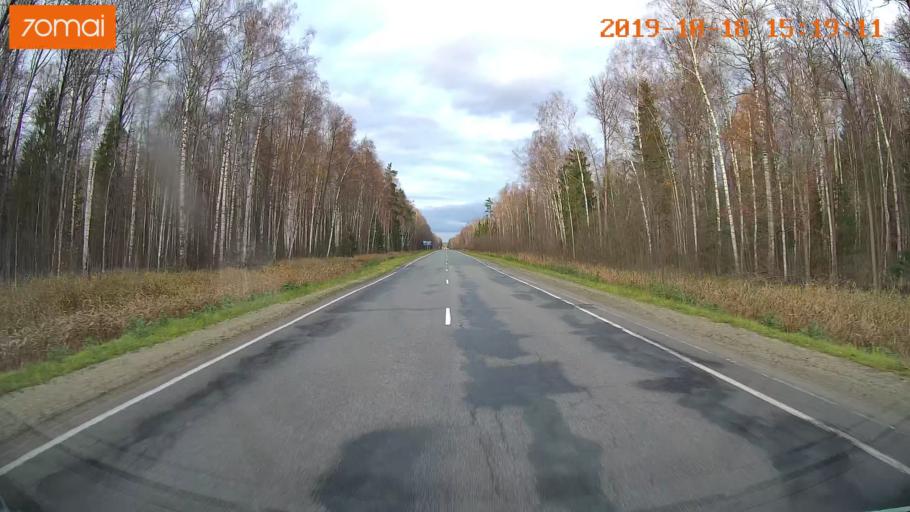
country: RU
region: Vladimir
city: Anopino
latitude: 55.6692
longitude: 40.7357
